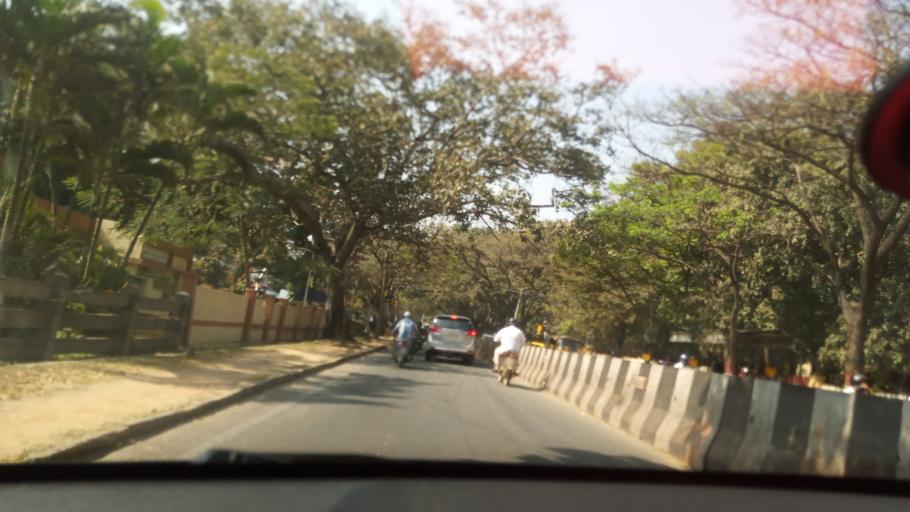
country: IN
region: Karnataka
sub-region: Bangalore Urban
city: Yelahanka
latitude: 13.0490
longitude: 77.5542
